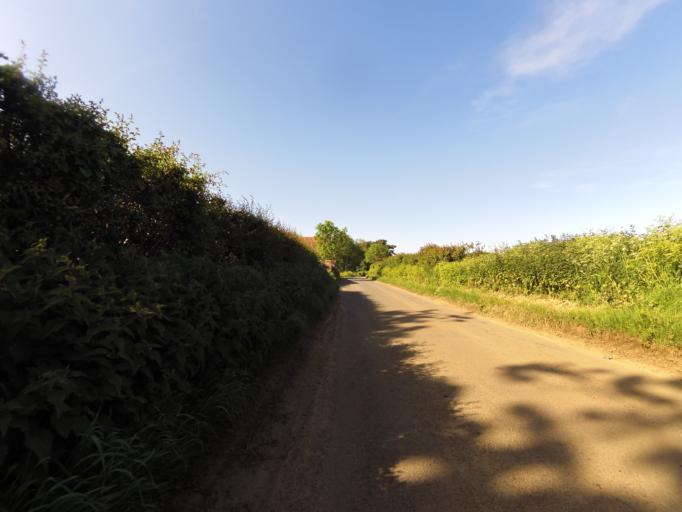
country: GB
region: England
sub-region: Suffolk
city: Felixstowe
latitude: 51.9978
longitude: 1.4129
